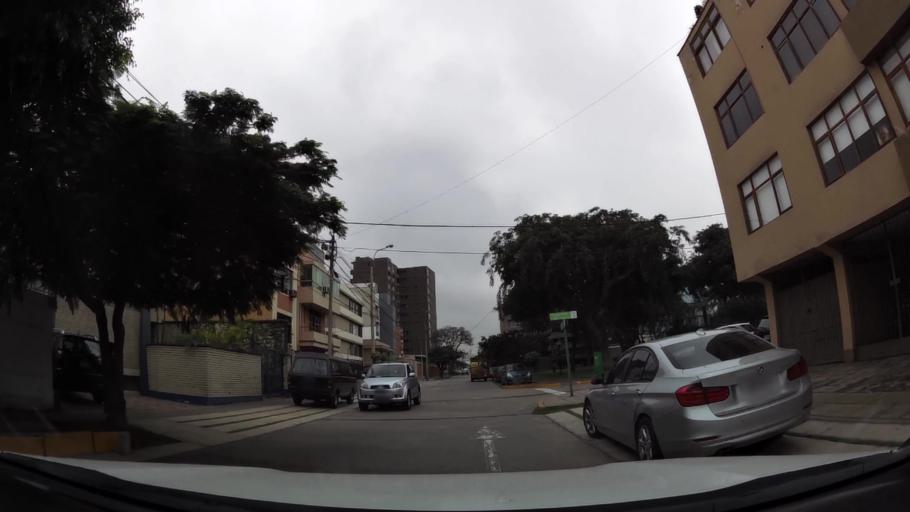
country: PE
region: Lima
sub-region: Lima
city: Surco
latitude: -12.1279
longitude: -77.0173
